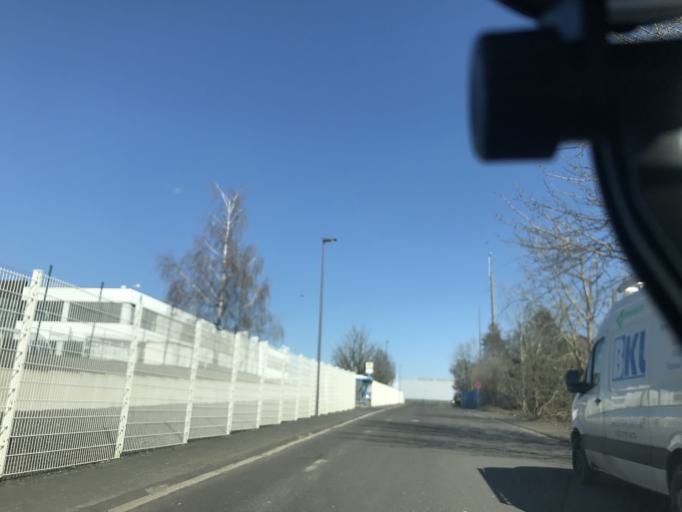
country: DE
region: Rheinland-Pfalz
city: Aach
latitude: 49.7754
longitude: 6.5822
